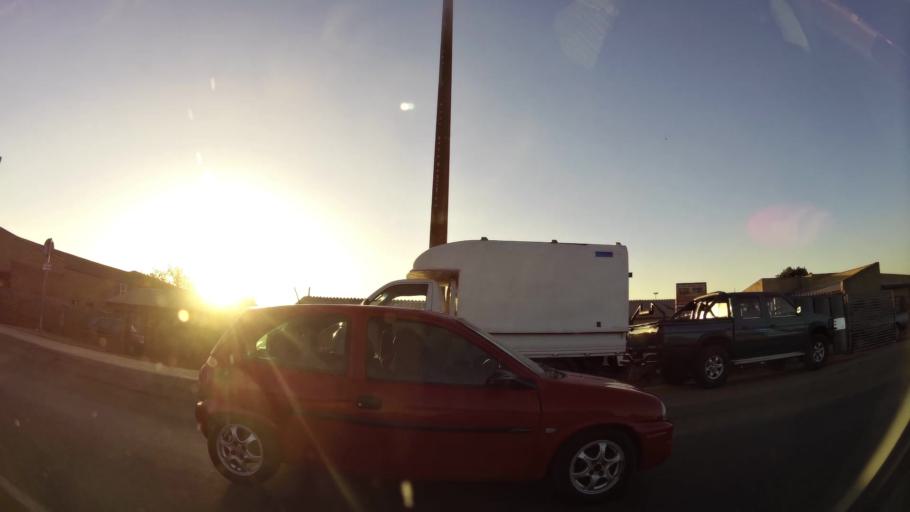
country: ZA
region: Gauteng
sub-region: Ekurhuleni Metropolitan Municipality
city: Tembisa
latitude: -26.0007
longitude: 28.2233
